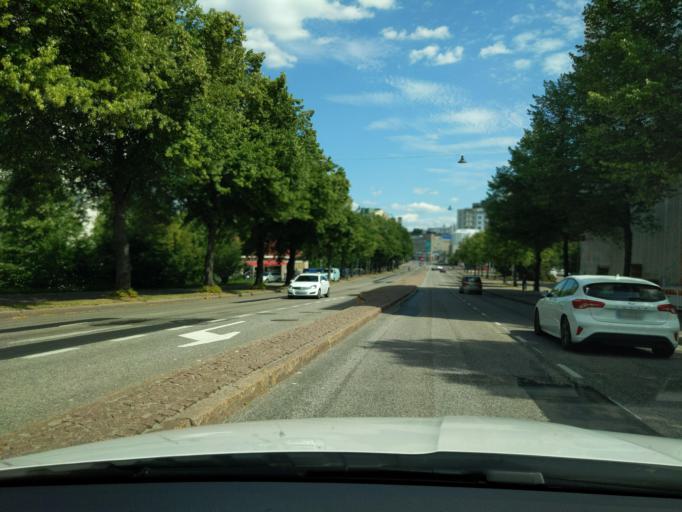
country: FI
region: Paijanne Tavastia
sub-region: Lahti
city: Lahti
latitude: 60.9820
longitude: 25.6438
